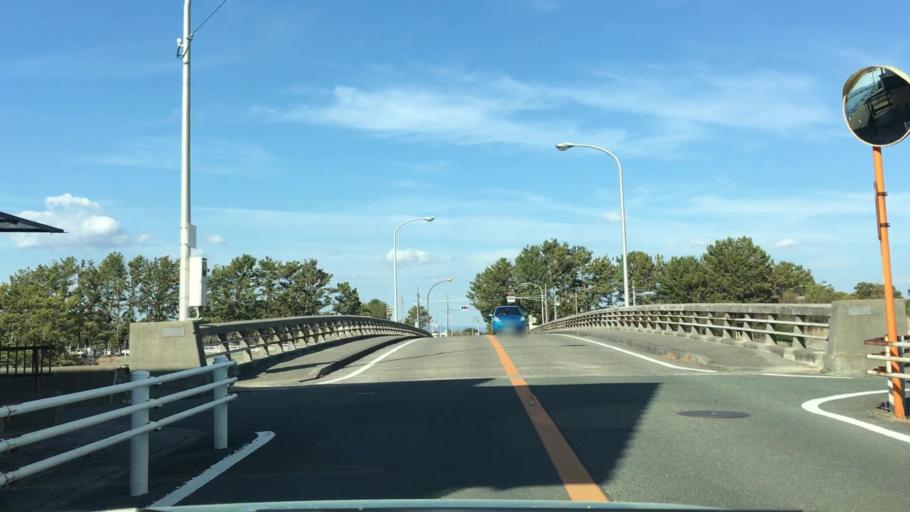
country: JP
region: Shizuoka
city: Kosai-shi
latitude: 34.6952
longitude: 137.6068
